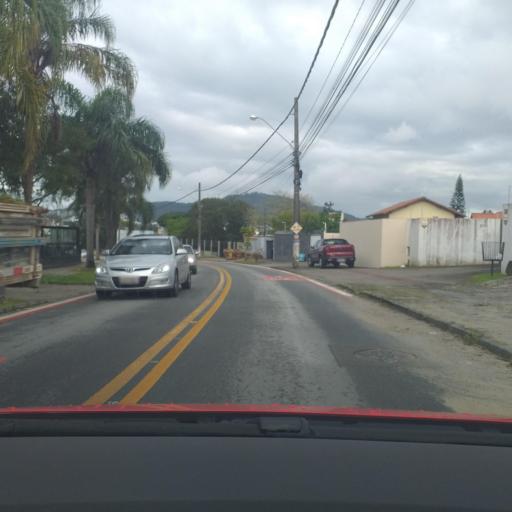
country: BR
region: Santa Catarina
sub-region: Florianopolis
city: Itacorubi
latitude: -27.5942
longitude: -48.4952
